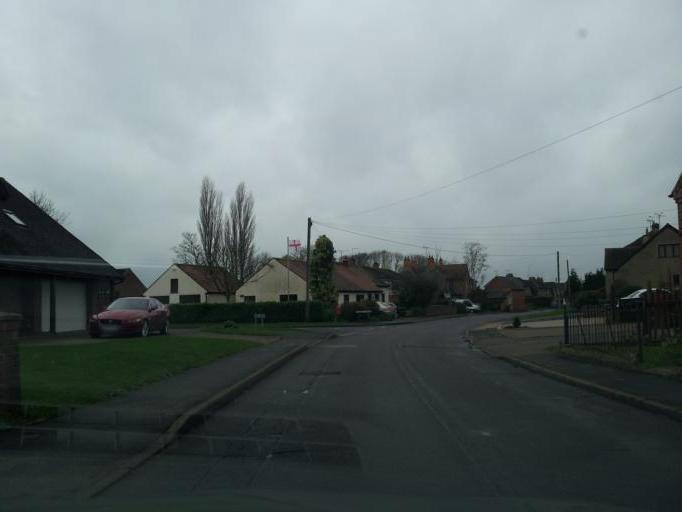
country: GB
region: England
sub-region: Warwickshire
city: Dunchurch
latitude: 52.3017
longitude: -1.2362
